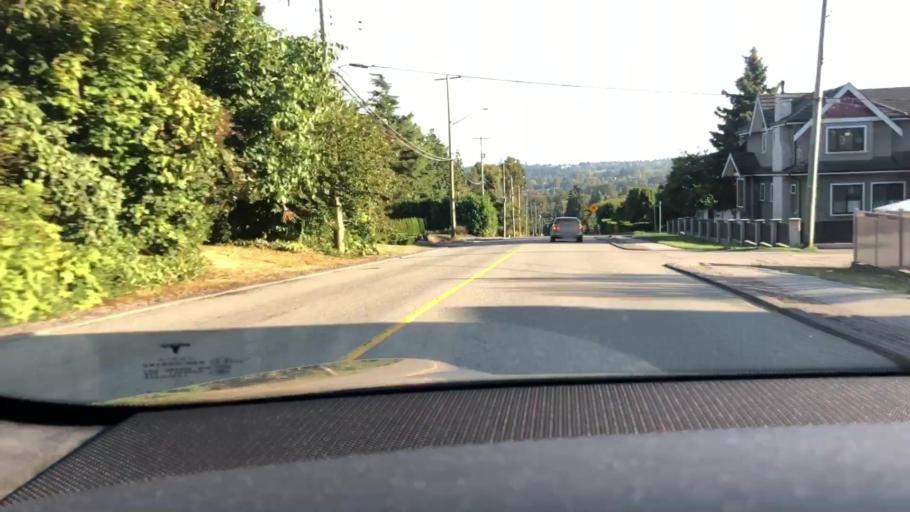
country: CA
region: British Columbia
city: Burnaby
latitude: 49.2669
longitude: -122.9702
